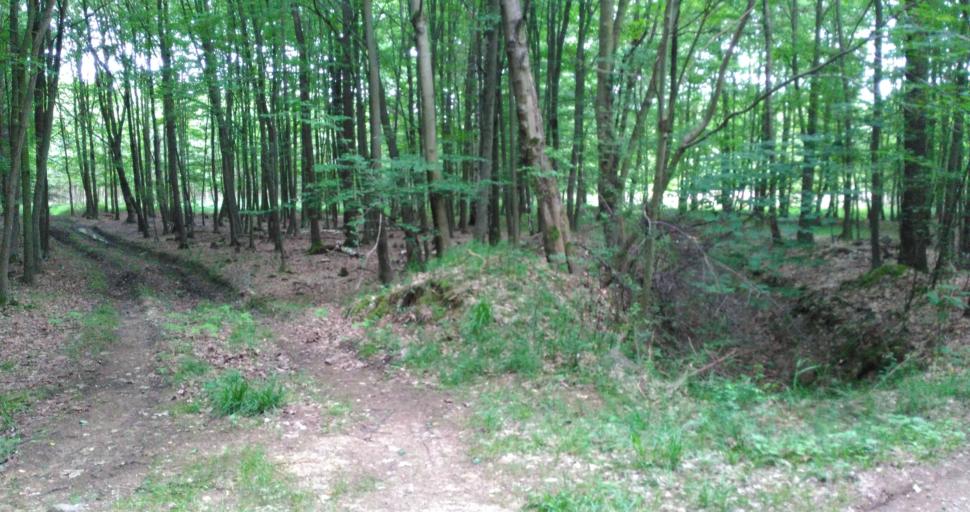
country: CZ
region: Central Bohemia
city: Zebrak
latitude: 49.9236
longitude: 13.8503
